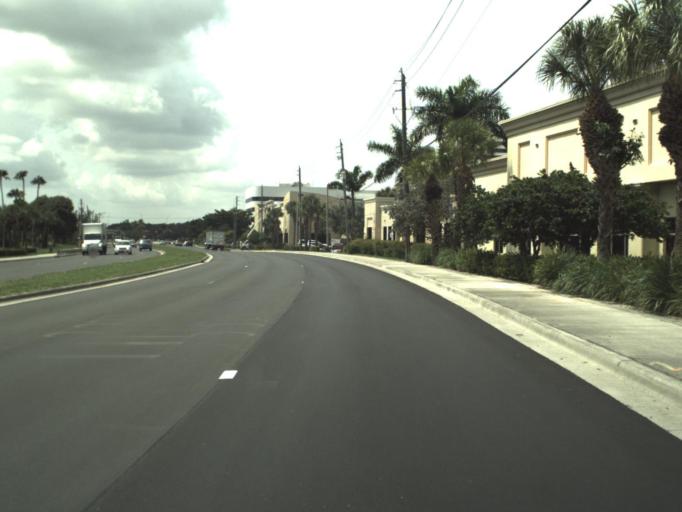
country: US
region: Florida
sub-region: Palm Beach County
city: West Palm Beach
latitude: 26.6951
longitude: -80.0749
